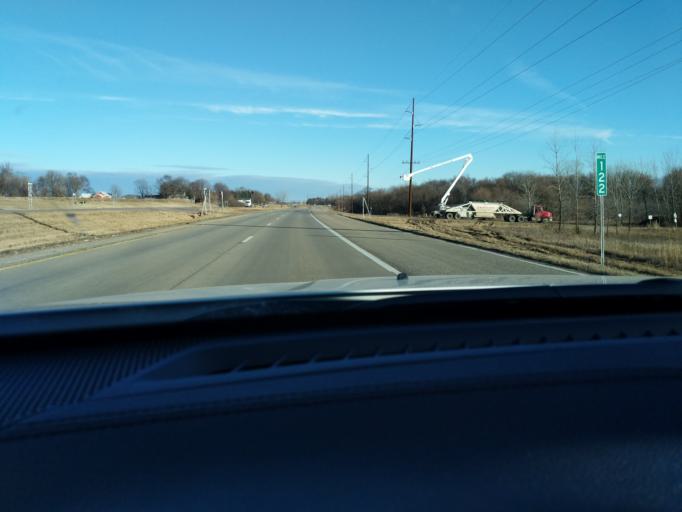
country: US
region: Minnesota
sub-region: McLeod County
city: Glencoe
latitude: 44.7687
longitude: -94.1178
